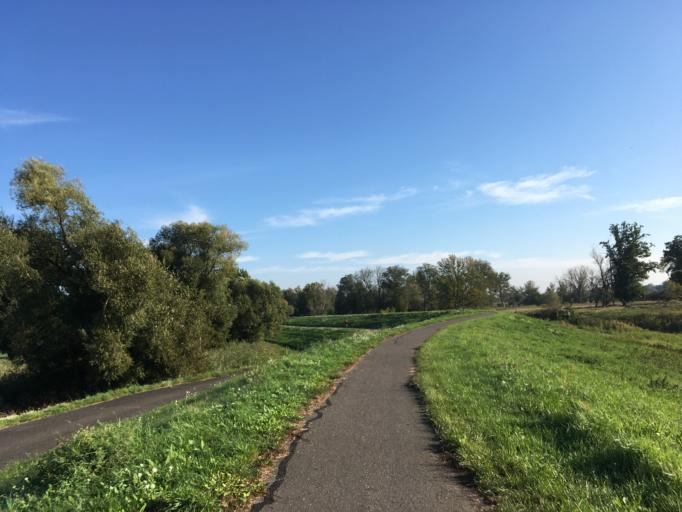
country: DE
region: Brandenburg
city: Lebus
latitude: 52.4449
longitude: 14.5754
